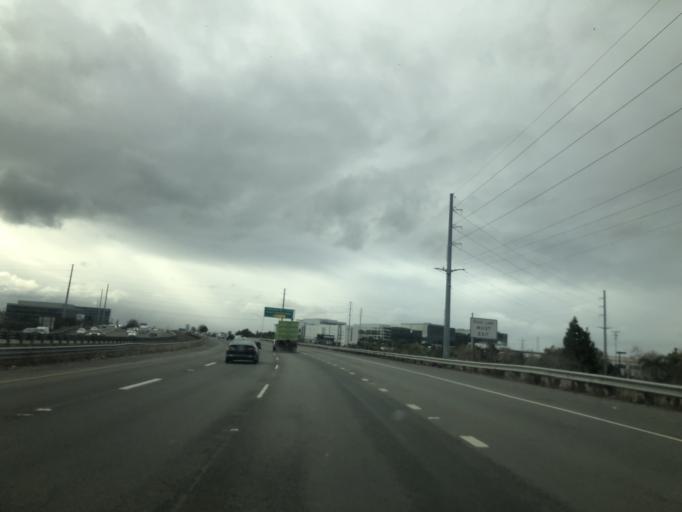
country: US
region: California
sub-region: Santa Clara County
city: Milpitas
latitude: 37.4179
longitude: -121.9690
